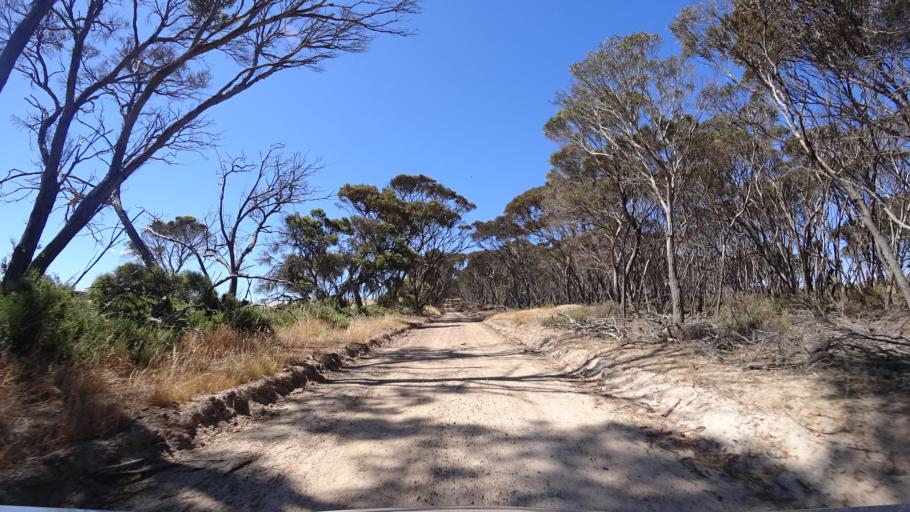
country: AU
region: South Australia
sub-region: Kangaroo Island
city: Kingscote
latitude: -35.7392
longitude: 137.7201
